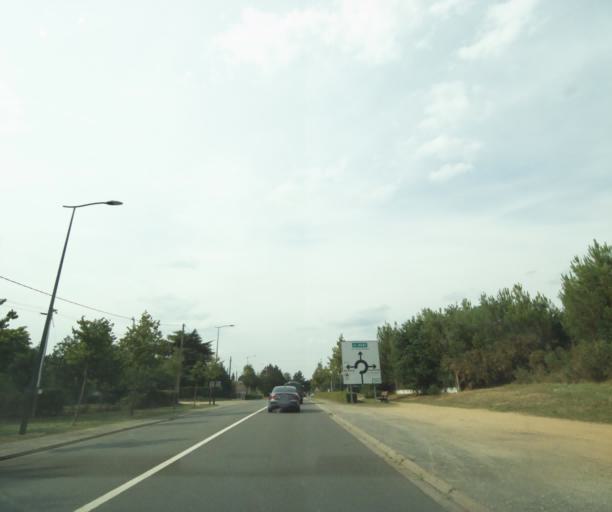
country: FR
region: Pays de la Loire
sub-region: Departement de la Sarthe
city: Mulsanne
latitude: 47.9115
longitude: 0.2442
